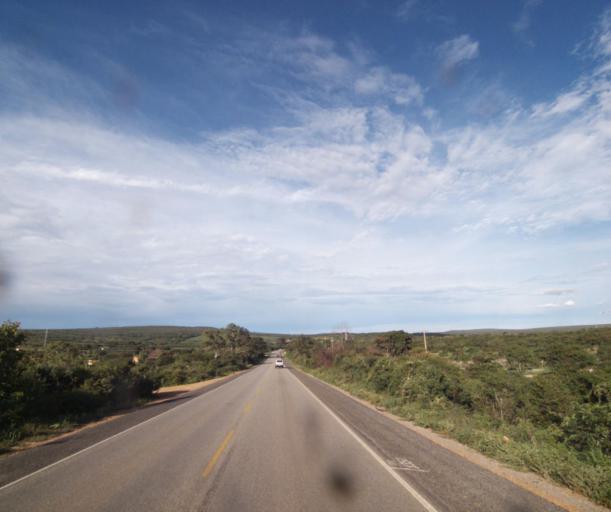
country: BR
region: Bahia
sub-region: Caetite
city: Caetite
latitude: -14.0888
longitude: -42.5703
